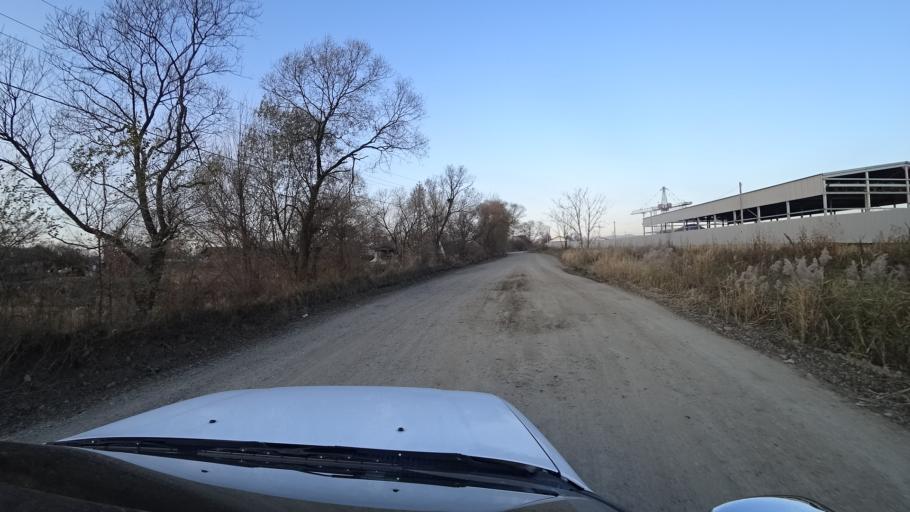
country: RU
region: Primorskiy
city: Dal'nerechensk
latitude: 45.9418
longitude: 133.8231
